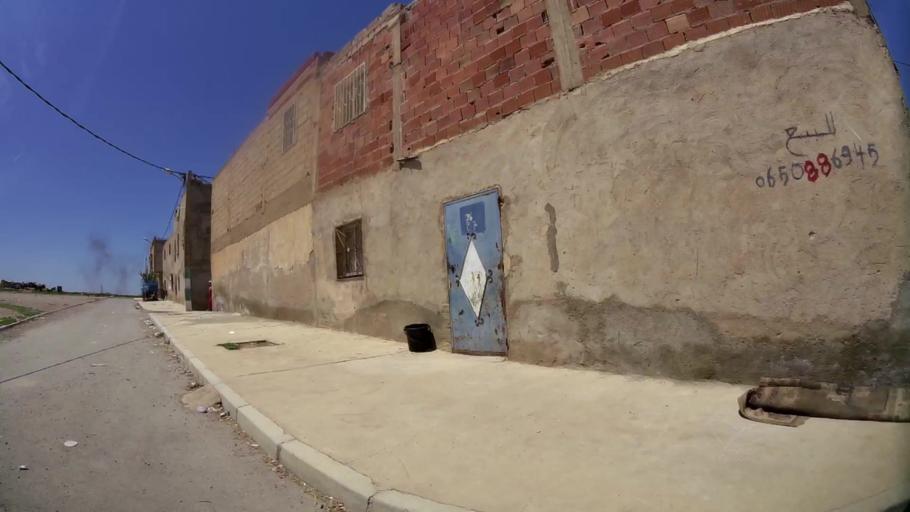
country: MA
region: Oriental
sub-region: Oujda-Angad
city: Oujda
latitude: 34.6931
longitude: -1.9482
